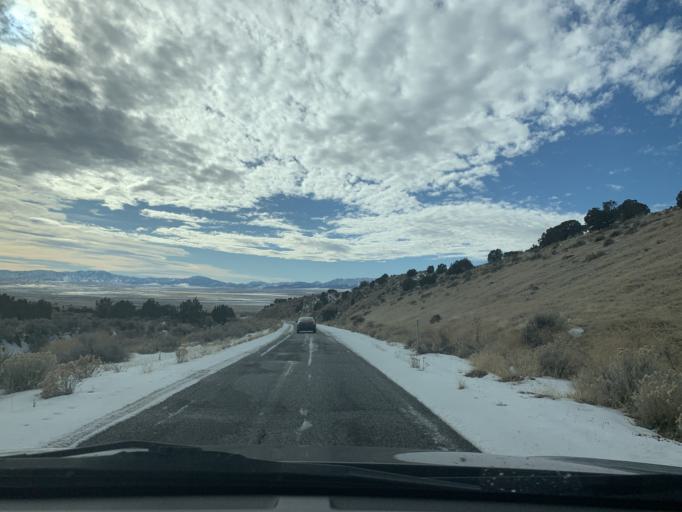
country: US
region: Utah
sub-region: Tooele County
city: Tooele
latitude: 40.3045
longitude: -112.2629
